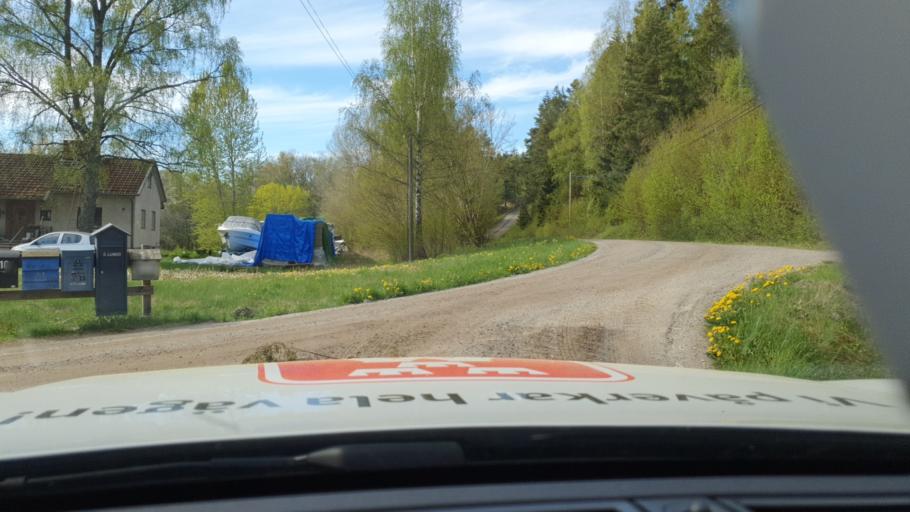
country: SE
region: Stockholm
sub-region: Haninge Kommun
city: Jordbro
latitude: 58.9996
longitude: 18.1414
